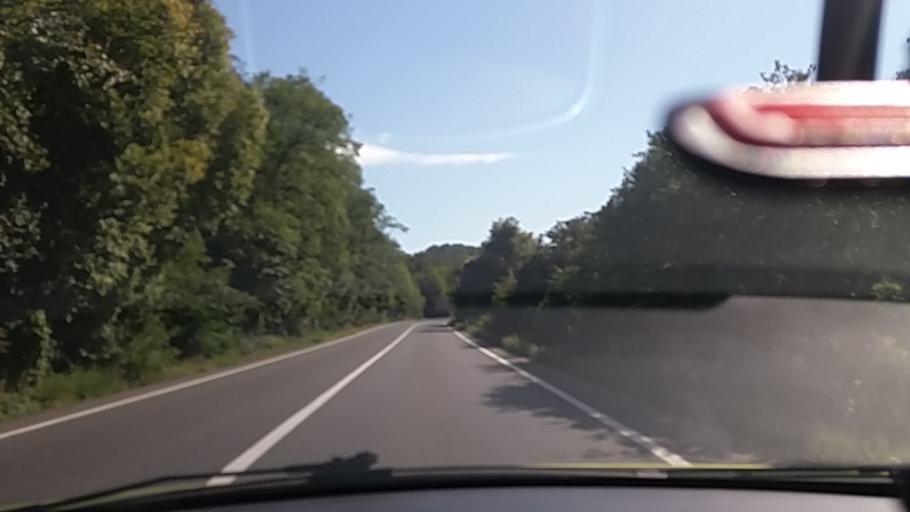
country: RO
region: Arad
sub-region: Comuna Ususau
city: Ususau
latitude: 46.1053
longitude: 21.7820
